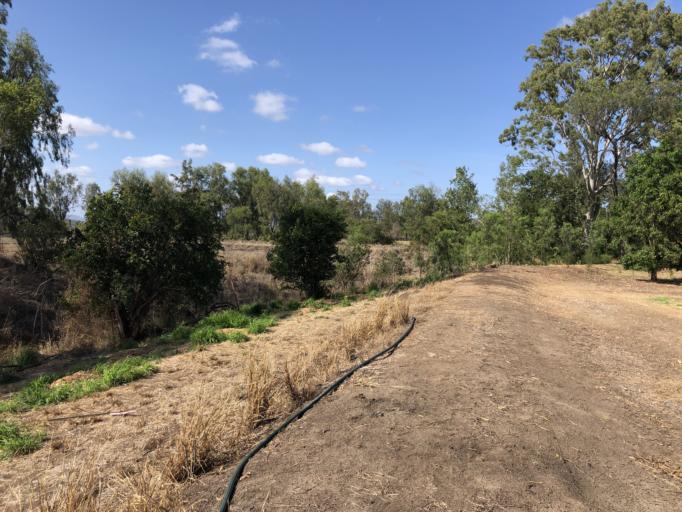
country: AU
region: Queensland
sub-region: Lockyer Valley
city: Gatton
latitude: -27.5869
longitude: 152.3459
